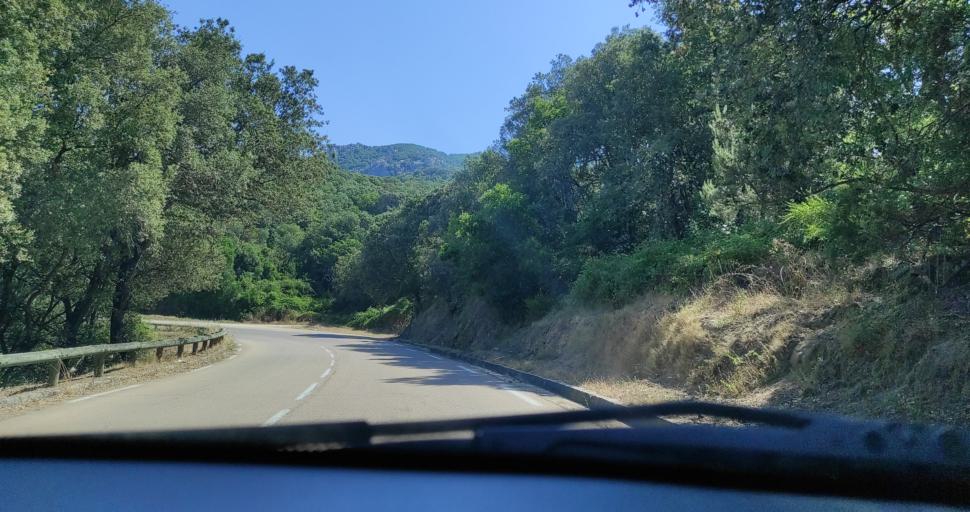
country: FR
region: Corsica
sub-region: Departement de la Corse-du-Sud
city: Sartene
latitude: 41.6079
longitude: 8.9432
